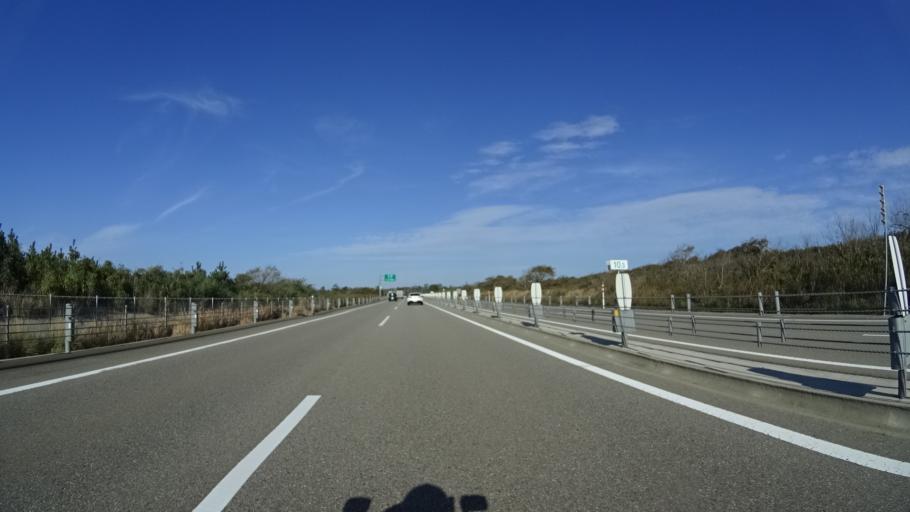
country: JP
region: Ishikawa
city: Tsubata
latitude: 36.7093
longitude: 136.6786
